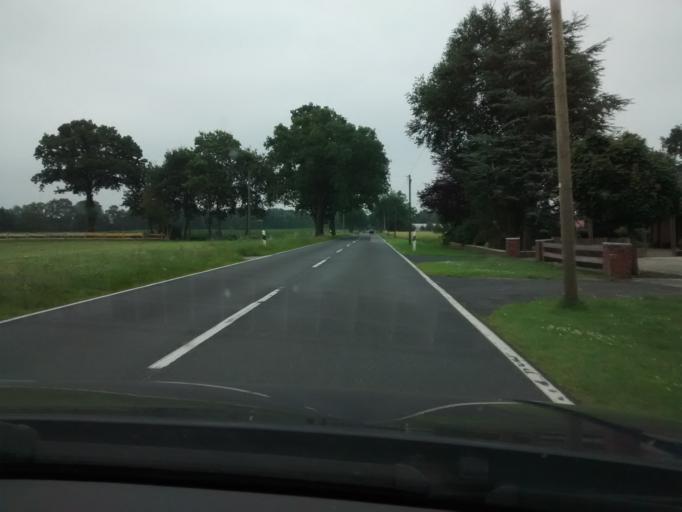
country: DE
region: Lower Saxony
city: Itterbeck
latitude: 52.5395
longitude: 6.7983
